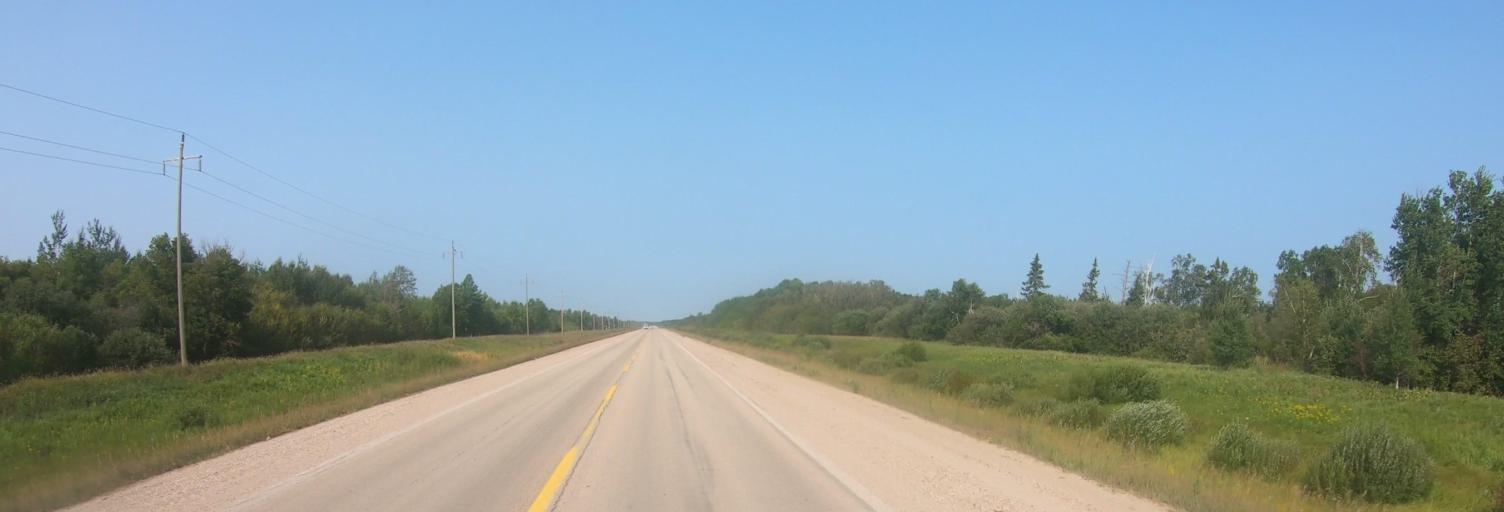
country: US
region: Minnesota
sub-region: Roseau County
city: Roseau
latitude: 49.0234
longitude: -95.6780
